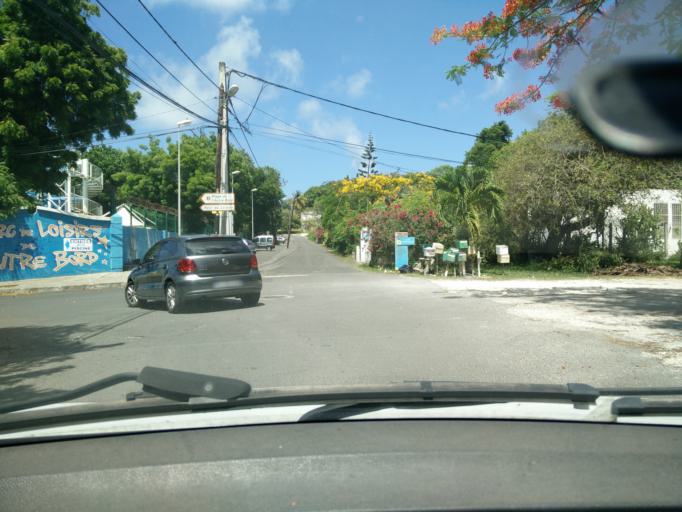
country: GP
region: Guadeloupe
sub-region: Guadeloupe
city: Le Moule
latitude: 16.3310
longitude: -61.3392
